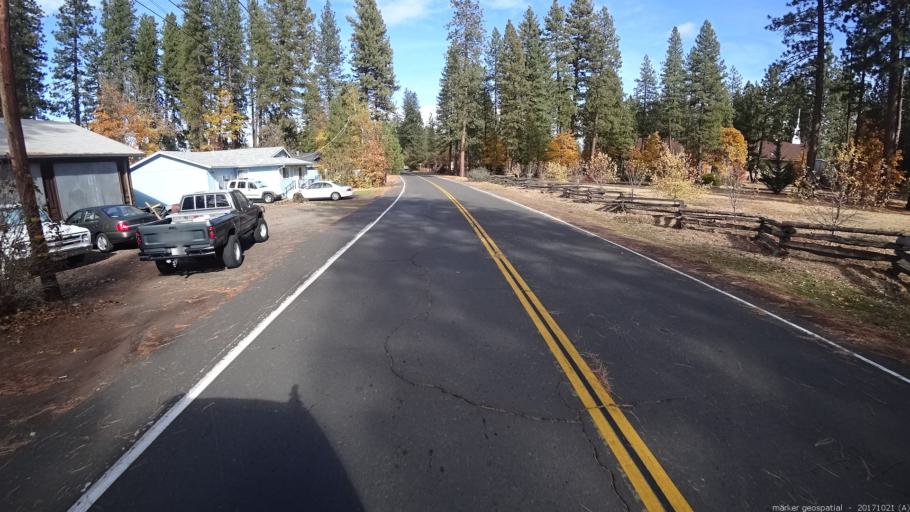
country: US
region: California
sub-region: Shasta County
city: Burney
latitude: 40.8820
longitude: -121.6594
